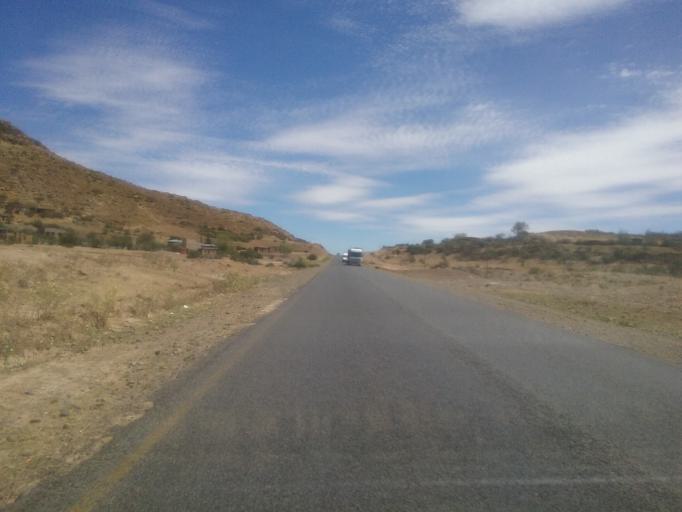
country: LS
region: Mohale's Hoek District
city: Mohale's Hoek
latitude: -30.0690
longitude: 27.4224
